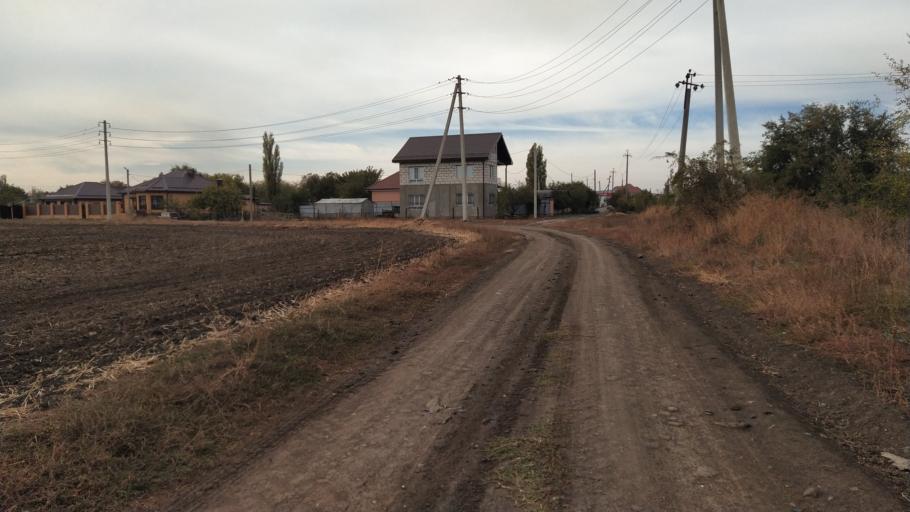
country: RU
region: Rostov
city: Bataysk
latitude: 47.1126
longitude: 39.6791
